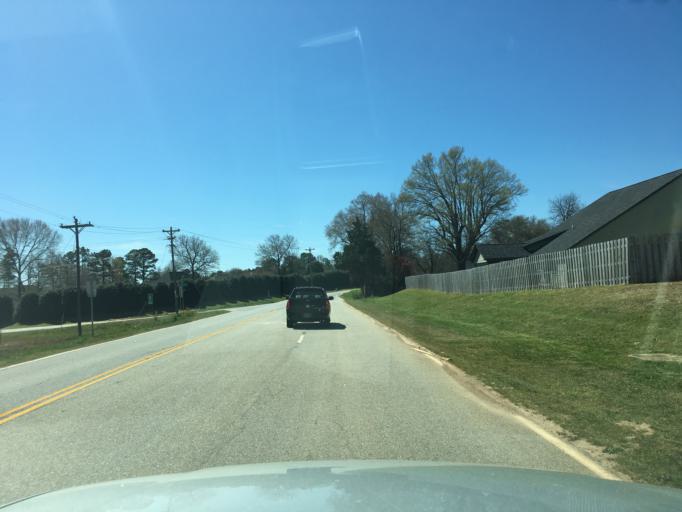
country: US
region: South Carolina
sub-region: Spartanburg County
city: Roebuck
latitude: 34.8929
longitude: -81.9681
